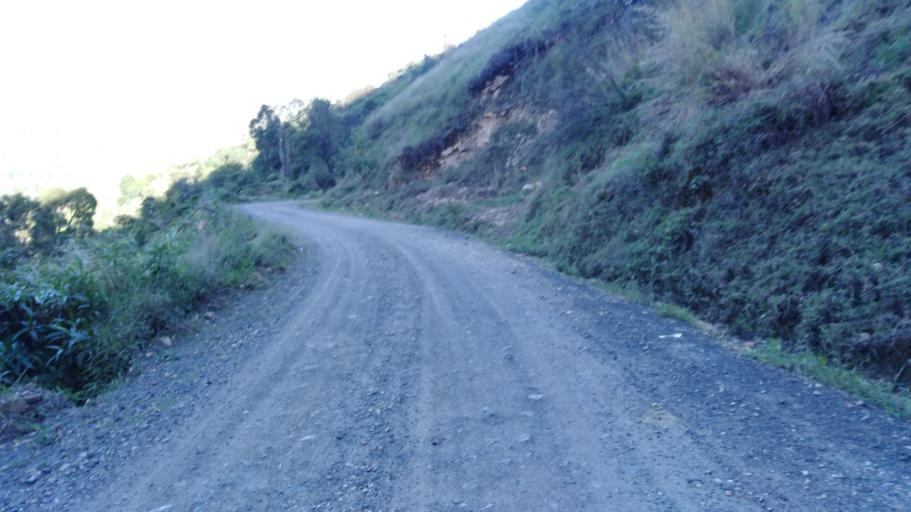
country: CO
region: Boyaca
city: San Mateo
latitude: 6.4019
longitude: -72.5632
